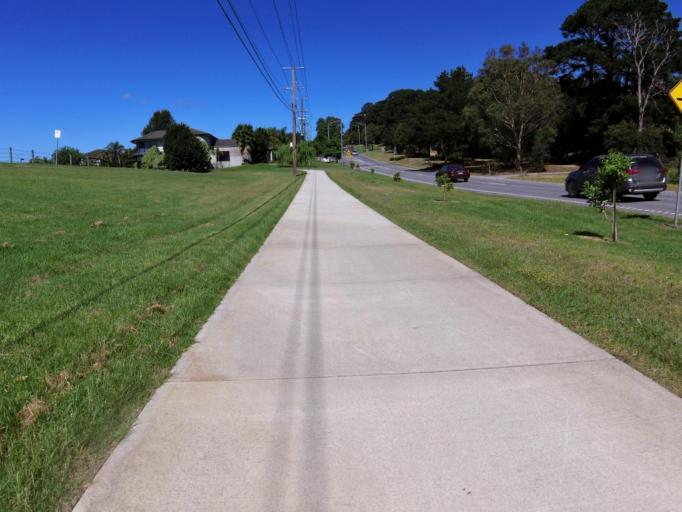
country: AU
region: Victoria
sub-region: Casey
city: Endeavour Hills
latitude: -37.9588
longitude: 145.2693
